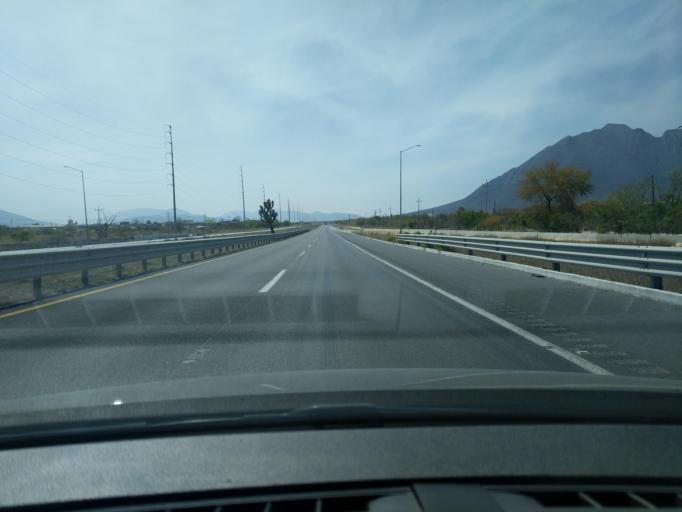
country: MX
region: Nuevo Leon
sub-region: General Escobedo
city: Praderas de San Francisco
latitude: 25.8174
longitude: -100.3985
